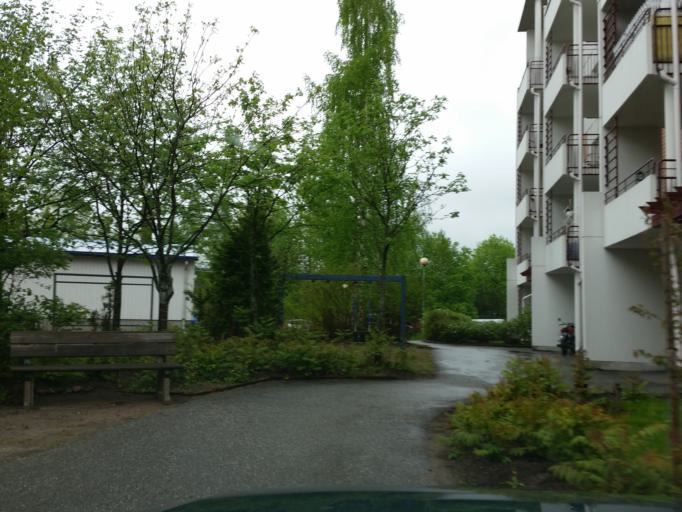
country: FI
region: Uusimaa
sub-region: Helsinki
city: Kilo
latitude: 60.2289
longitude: 24.8094
